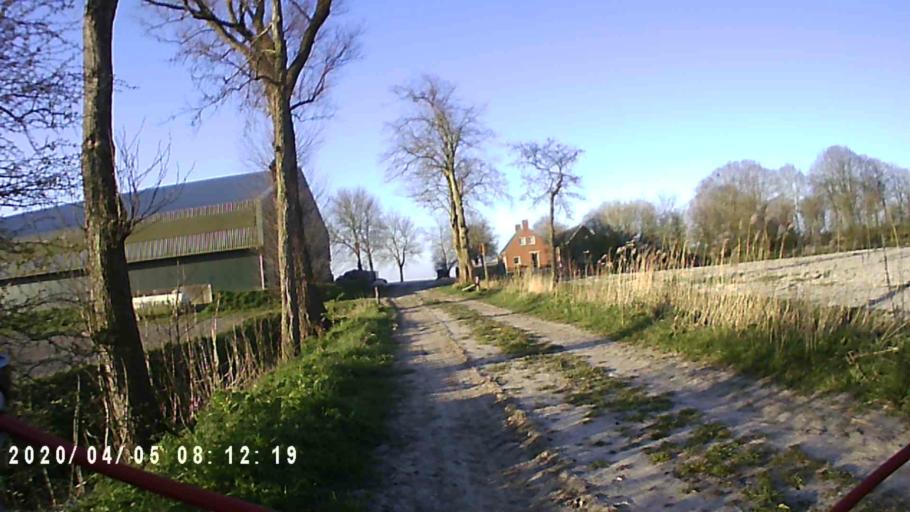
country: NL
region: Groningen
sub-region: Gemeente Zuidhorn
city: Oldehove
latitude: 53.3461
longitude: 6.4441
